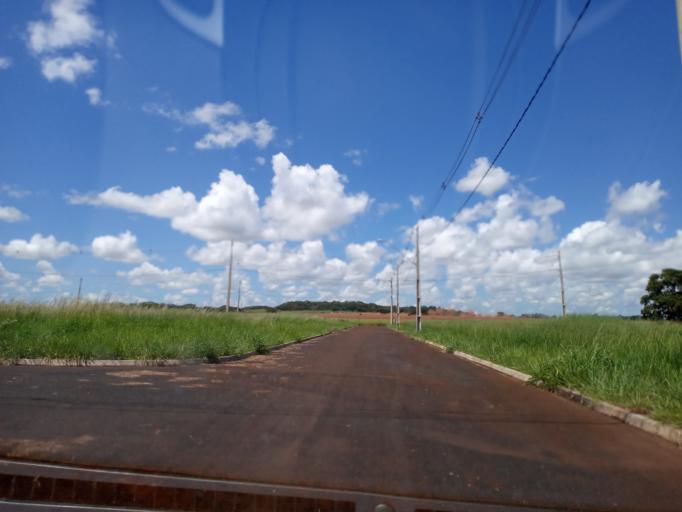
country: BR
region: Minas Gerais
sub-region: Centralina
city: Centralina
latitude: -18.5984
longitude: -49.1991
